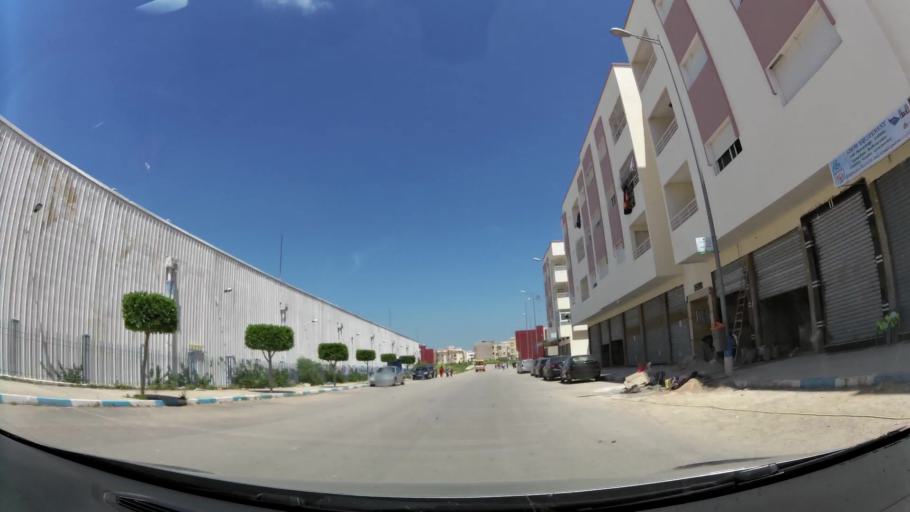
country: MA
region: Fes-Boulemane
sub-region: Fes
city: Fes
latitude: 34.0214
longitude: -5.0527
